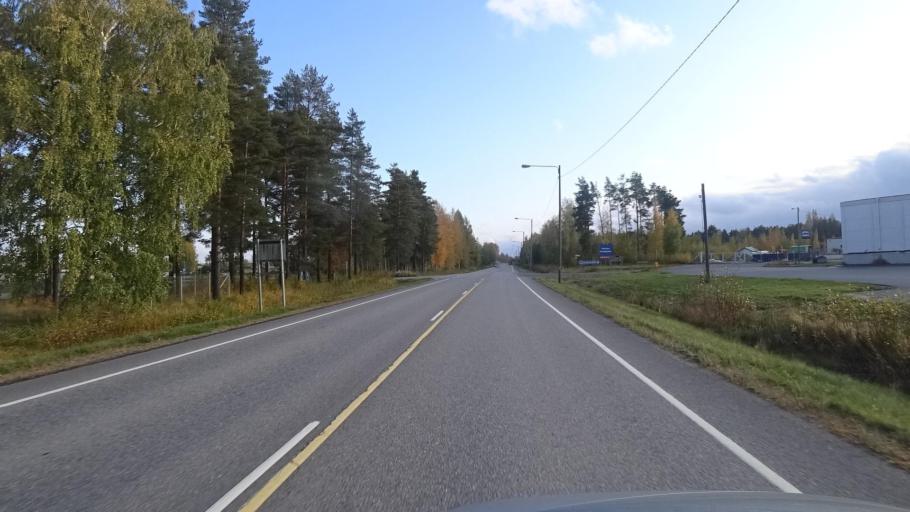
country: FI
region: Satakunta
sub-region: Rauma
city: Saekylae
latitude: 61.0637
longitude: 22.3241
